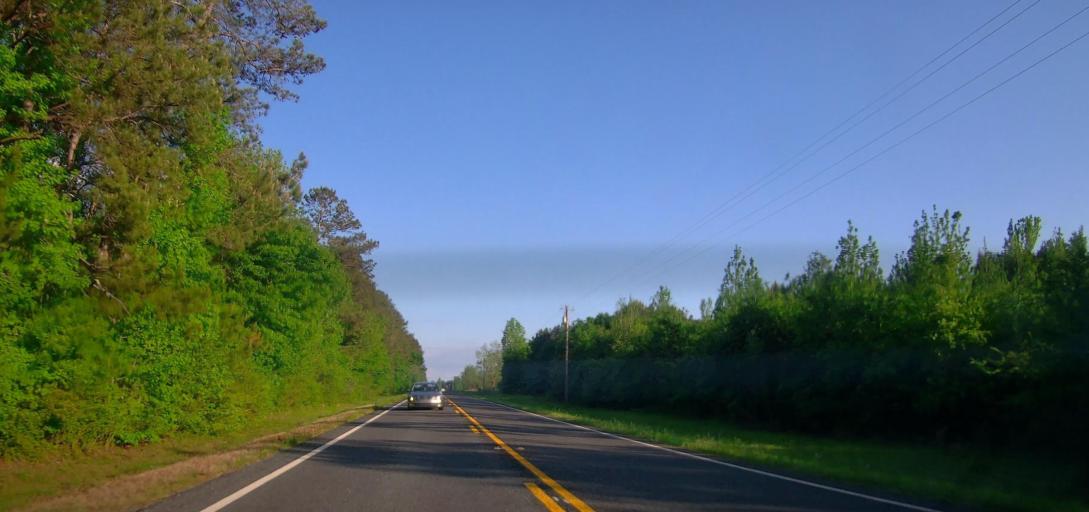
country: US
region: Georgia
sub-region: Jasper County
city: Monticello
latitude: 33.4245
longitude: -83.6156
